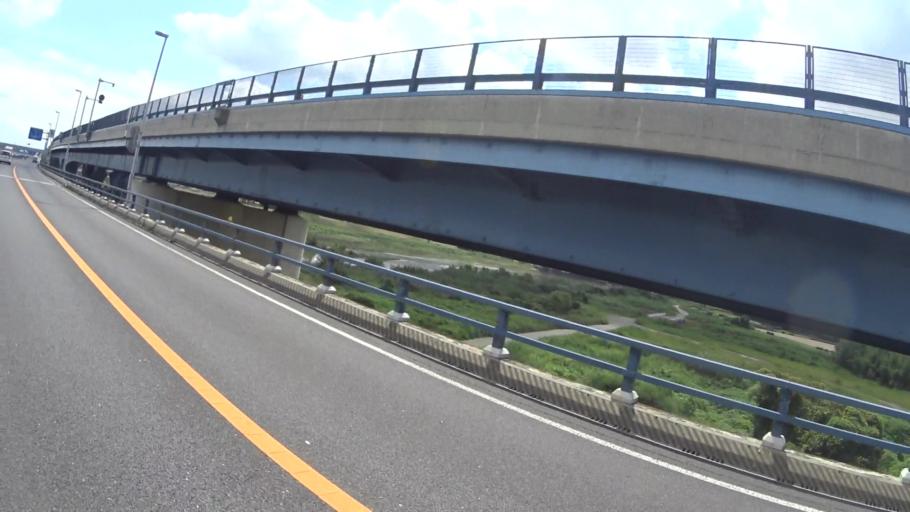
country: JP
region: Kyoto
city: Yawata
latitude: 34.8994
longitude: 135.7000
